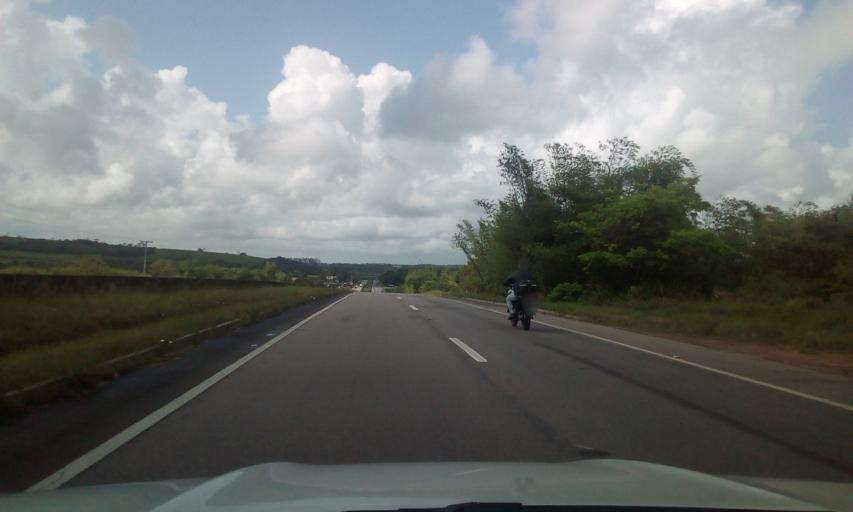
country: BR
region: Paraiba
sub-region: Alhandra
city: Alhandra
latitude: -7.3899
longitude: -34.9565
